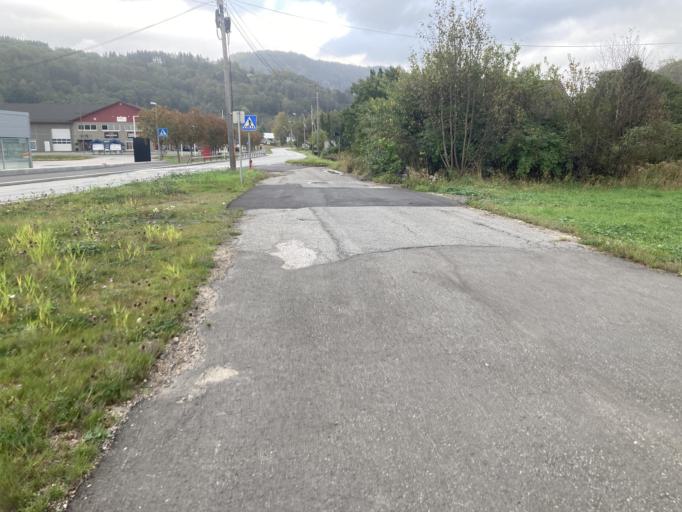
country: NO
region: Vest-Agder
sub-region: Kvinesdal
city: Liknes
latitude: 58.3205
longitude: 6.9655
